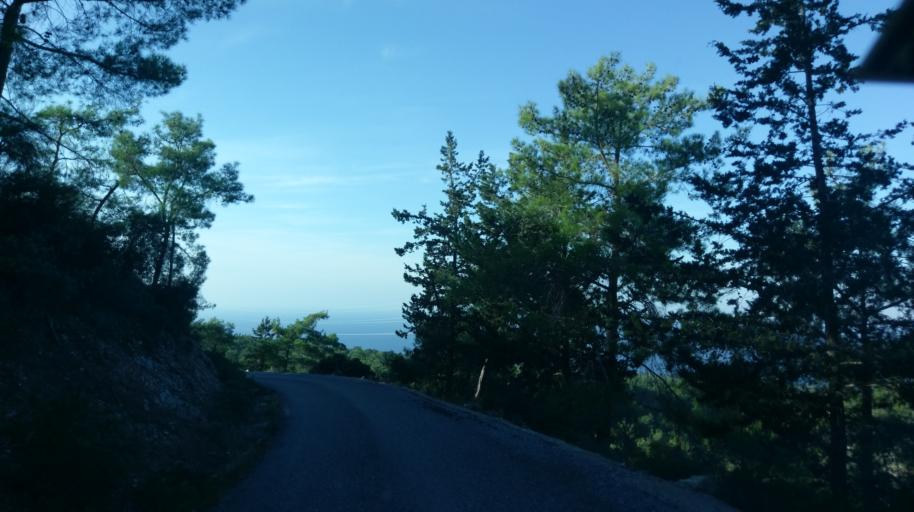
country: CY
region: Ammochostos
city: Lefkonoiko
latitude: 35.3261
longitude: 33.6070
